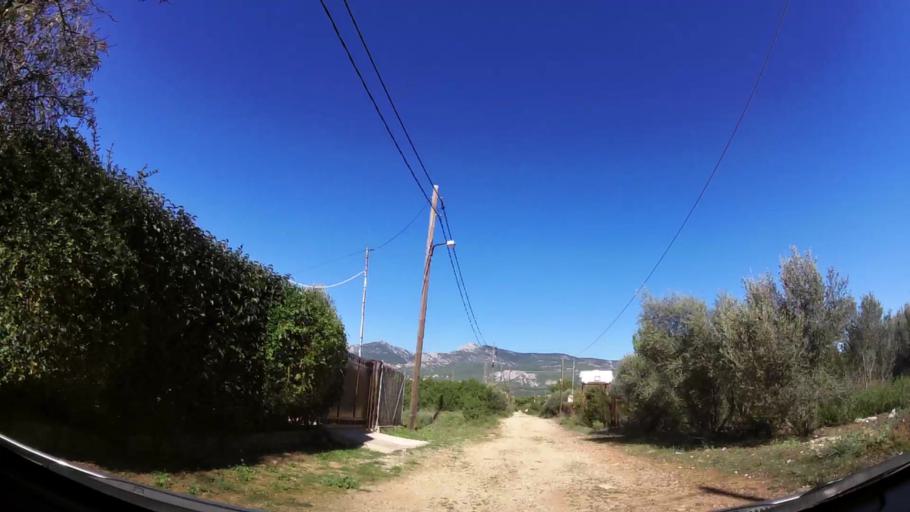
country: GR
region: Attica
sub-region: Nomarchia Anatolikis Attikis
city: Varybobi
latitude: 38.1213
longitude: 23.7851
